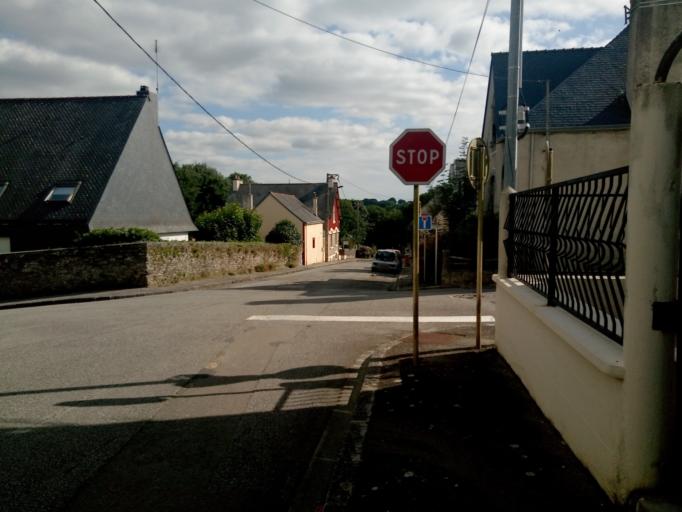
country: FR
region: Brittany
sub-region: Departement du Morbihan
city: Gourin
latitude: 48.1385
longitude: -3.6053
